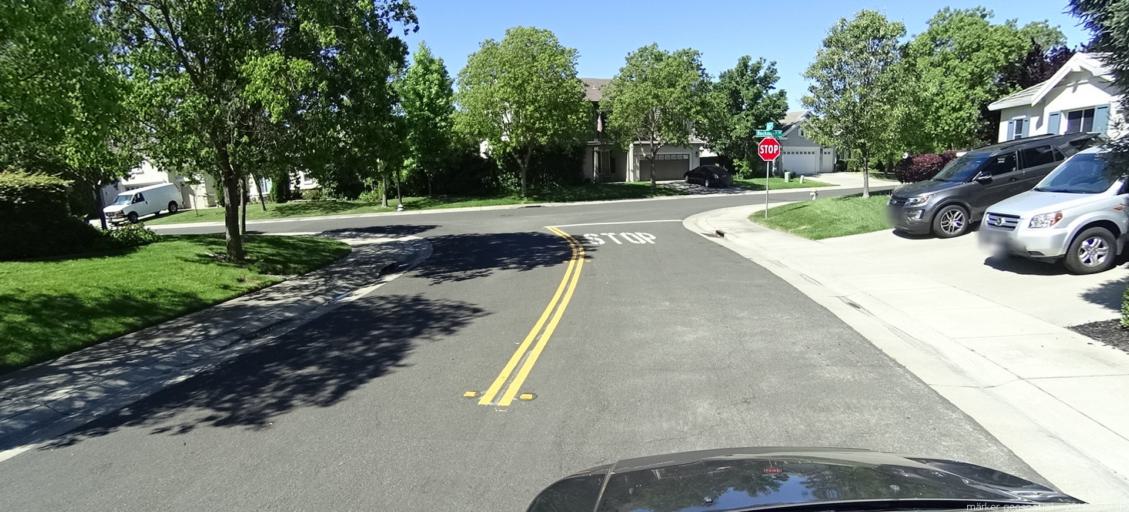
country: US
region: California
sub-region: Sacramento County
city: Elverta
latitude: 38.6747
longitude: -121.5199
